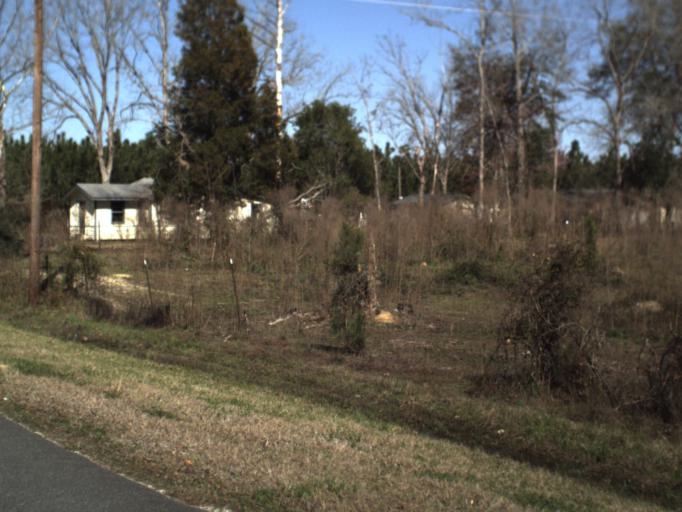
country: US
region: Florida
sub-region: Calhoun County
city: Blountstown
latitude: 30.3054
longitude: -85.1286
